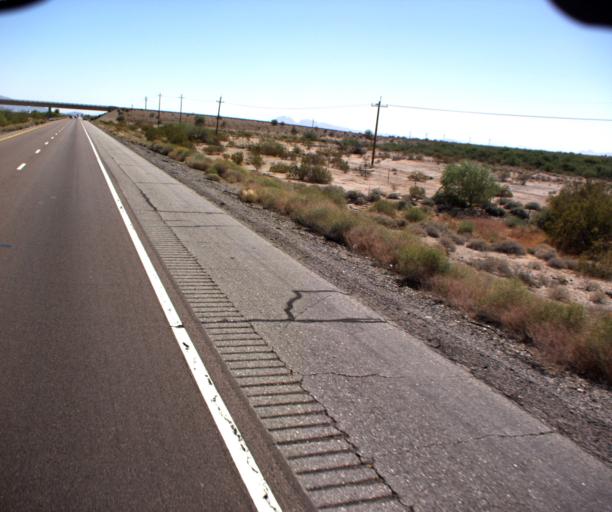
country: US
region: Arizona
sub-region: La Paz County
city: Salome
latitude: 33.5613
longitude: -113.3041
